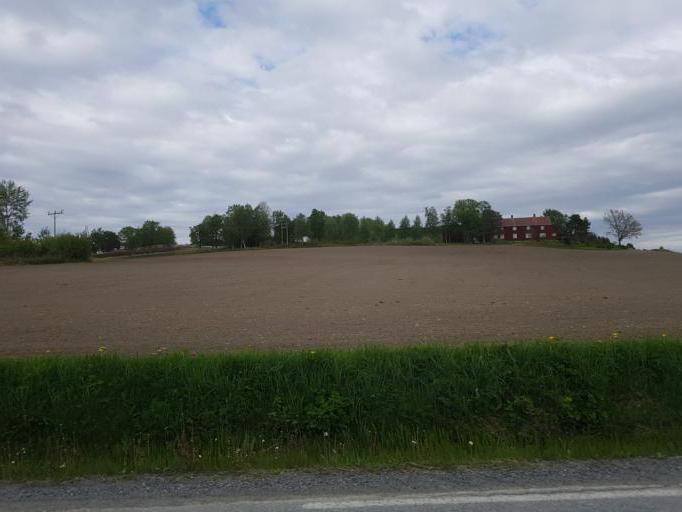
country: NO
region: Nord-Trondelag
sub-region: Levanger
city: Skogn
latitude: 63.7018
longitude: 11.2345
